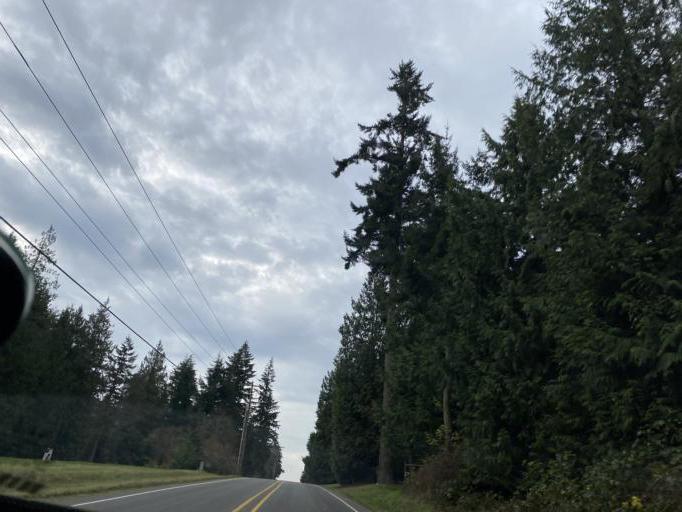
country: US
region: Washington
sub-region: Island County
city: Freeland
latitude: 47.9992
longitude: -122.5370
